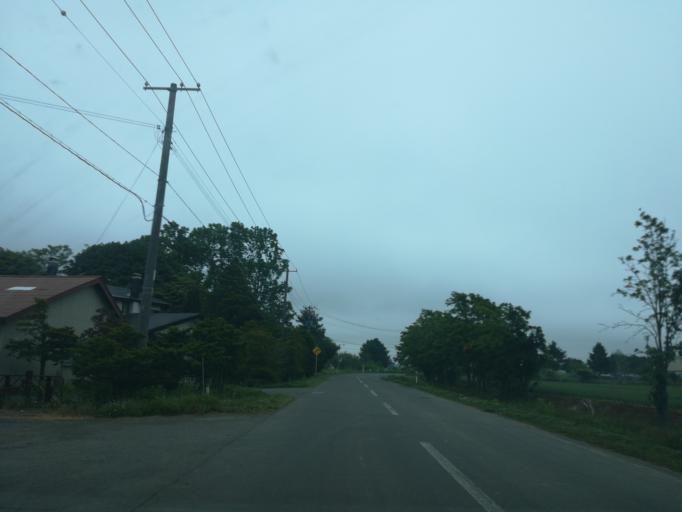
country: JP
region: Hokkaido
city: Ebetsu
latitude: 43.0712
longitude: 141.6440
